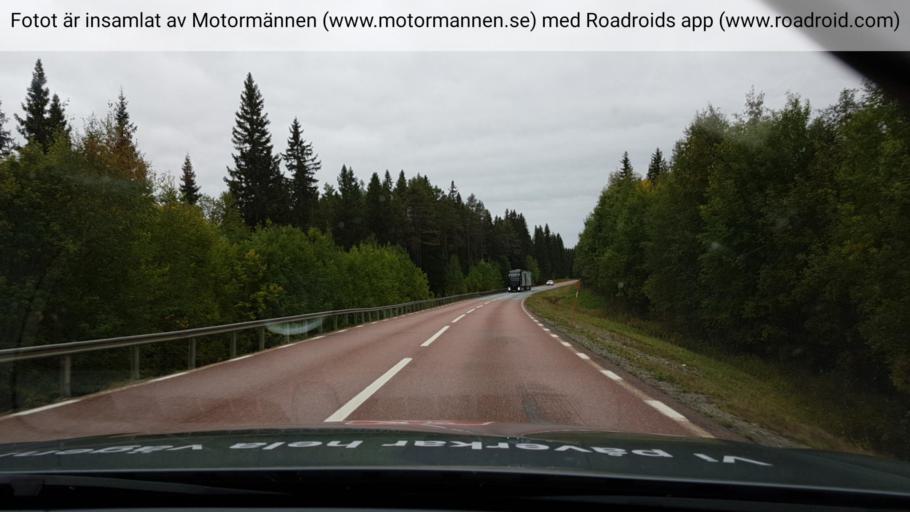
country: SE
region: Vaesterbotten
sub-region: Dorotea Kommun
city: Dorotea
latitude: 64.1512
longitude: 16.2609
